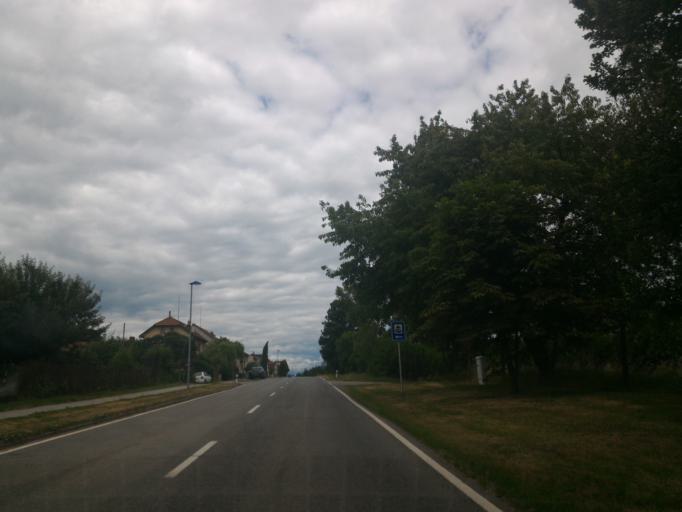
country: CZ
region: Vysocina
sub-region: Okres Pelhrimov
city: Zeliv
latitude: 49.5149
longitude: 15.1767
